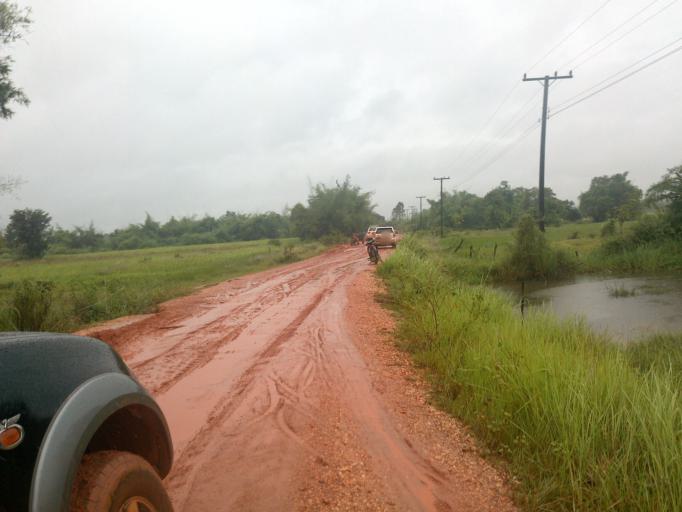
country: TH
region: Changwat Bueng Kan
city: Bung Khla
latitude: 18.3370
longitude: 103.8601
